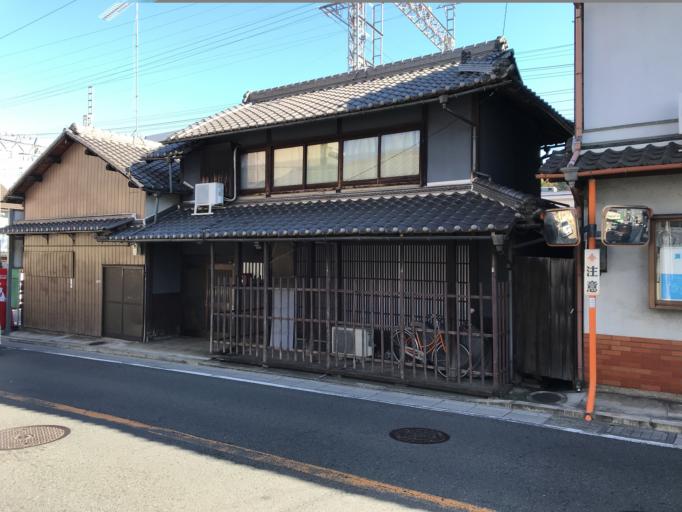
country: JP
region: Osaka
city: Tondabayashicho
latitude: 34.4526
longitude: 135.5734
